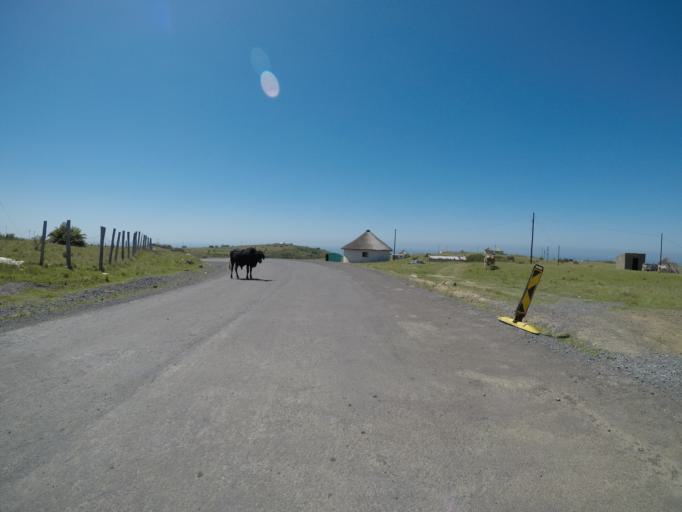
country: ZA
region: Eastern Cape
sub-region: OR Tambo District Municipality
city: Libode
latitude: -32.0005
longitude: 29.1191
